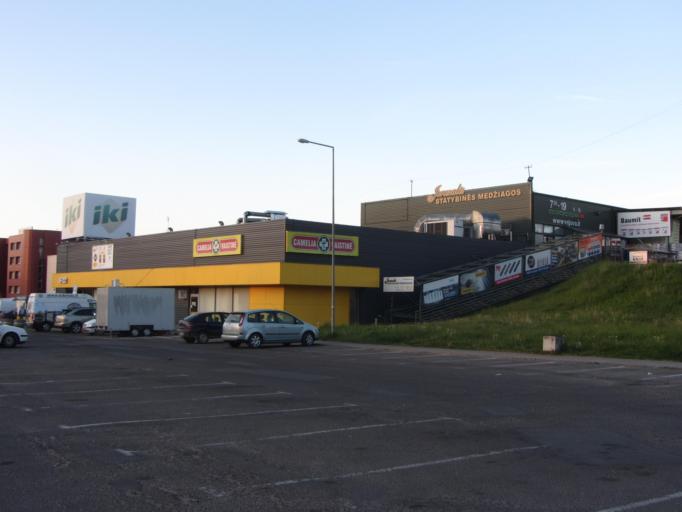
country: LT
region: Vilnius County
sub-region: Vilnius
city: Fabijoniskes
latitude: 54.7429
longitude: 25.2777
